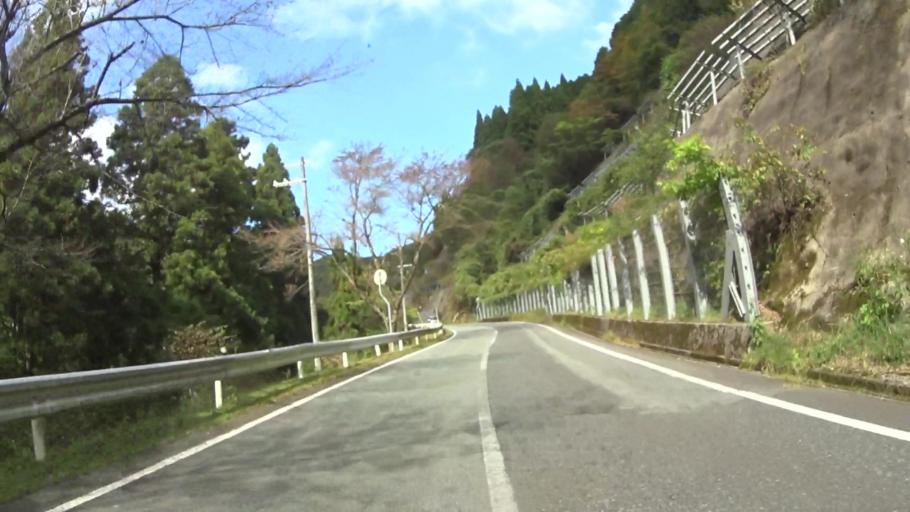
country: JP
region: Hyogo
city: Toyooka
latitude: 35.5160
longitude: 134.9903
